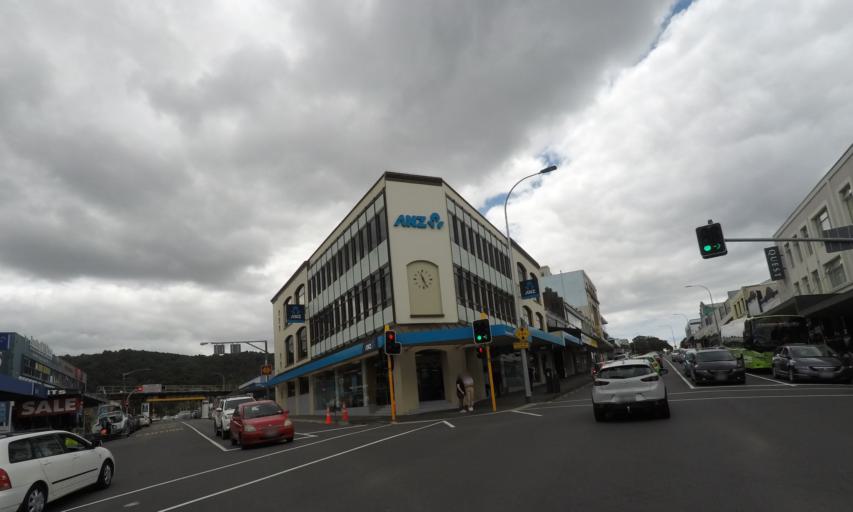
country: NZ
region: Northland
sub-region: Whangarei
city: Whangarei
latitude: -35.7248
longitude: 174.3195
